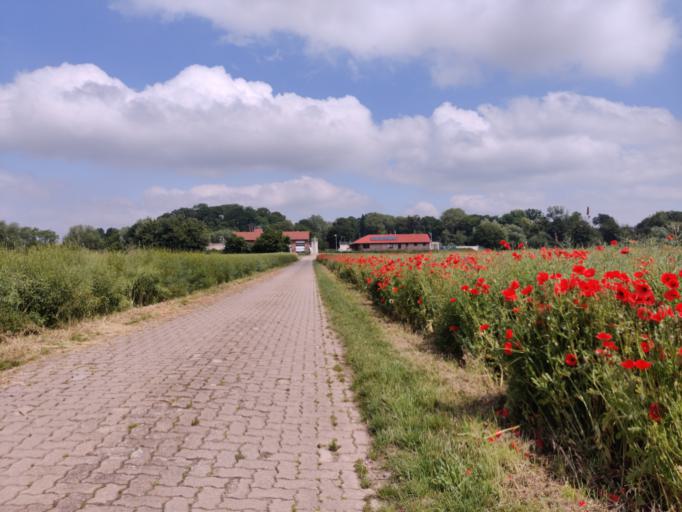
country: DE
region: Lower Saxony
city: Bad Salzdetfurth
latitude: 52.1016
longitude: 10.0104
